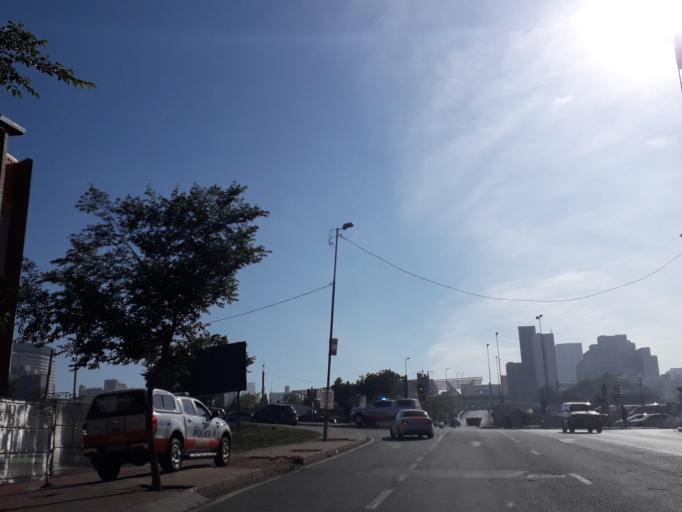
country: ZA
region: Gauteng
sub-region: City of Johannesburg Metropolitan Municipality
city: Johannesburg
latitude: -26.1995
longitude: 28.0350
